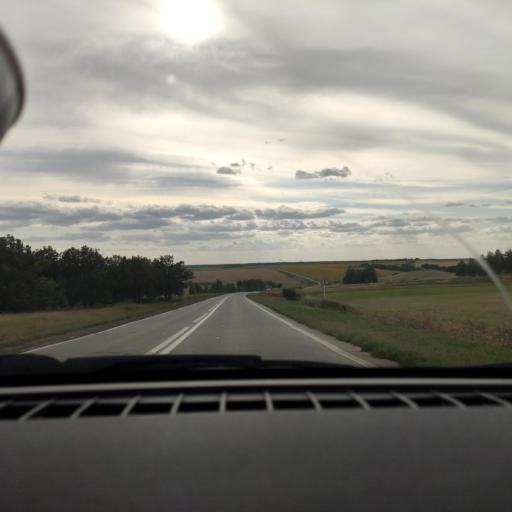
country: RU
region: Samara
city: Kinel'
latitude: 53.4414
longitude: 50.6286
